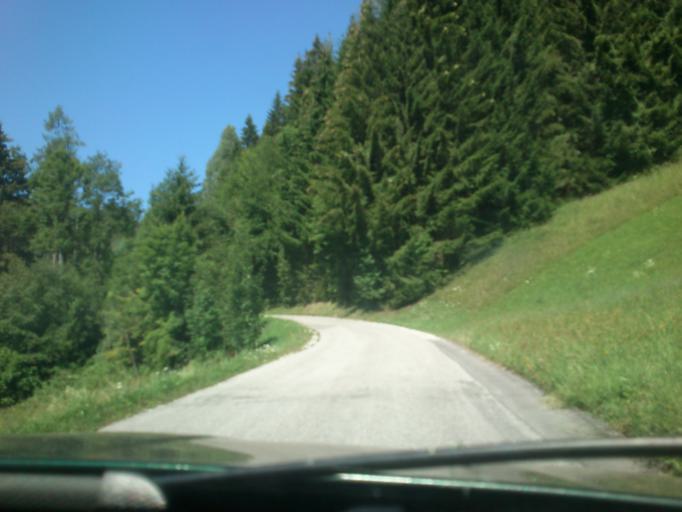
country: AT
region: Upper Austria
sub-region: Politischer Bezirk Kirchdorf an der Krems
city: Rossleithen
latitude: 47.7240
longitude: 14.3621
